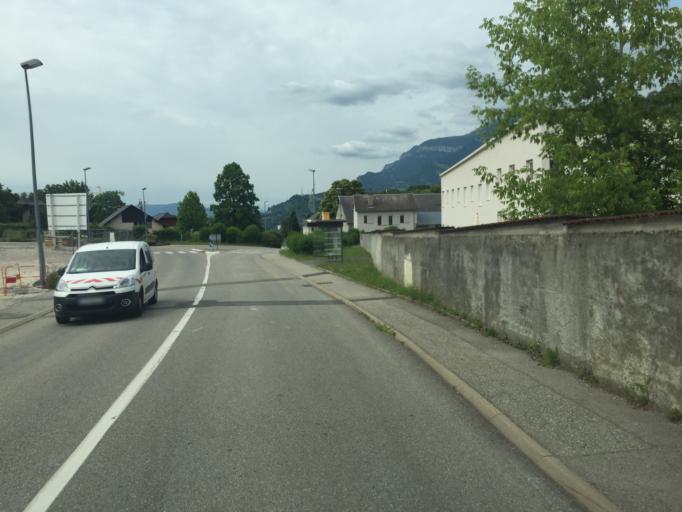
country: FR
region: Rhone-Alpes
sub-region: Departement de la Savoie
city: Jacob-Bellecombette
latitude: 45.5526
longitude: 5.9215
